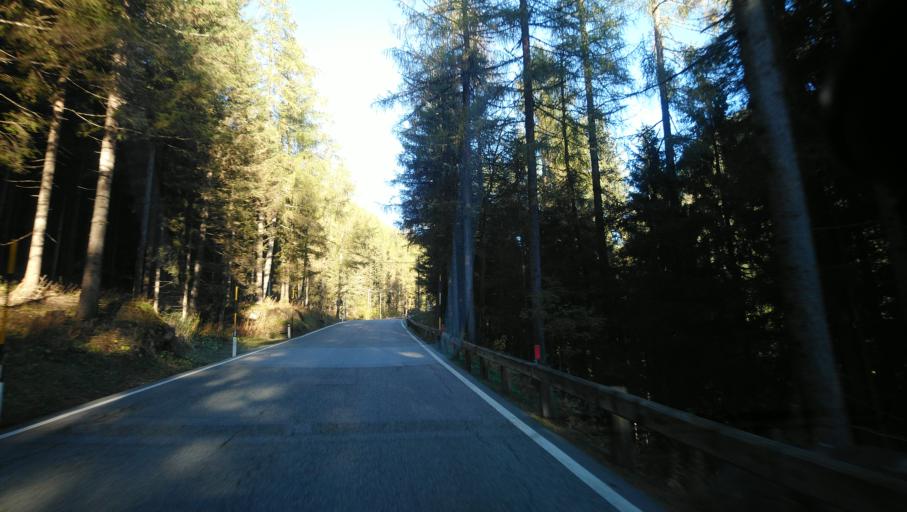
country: IT
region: Veneto
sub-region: Provincia di Belluno
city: Falcade Alto
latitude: 46.3654
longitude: 11.8330
